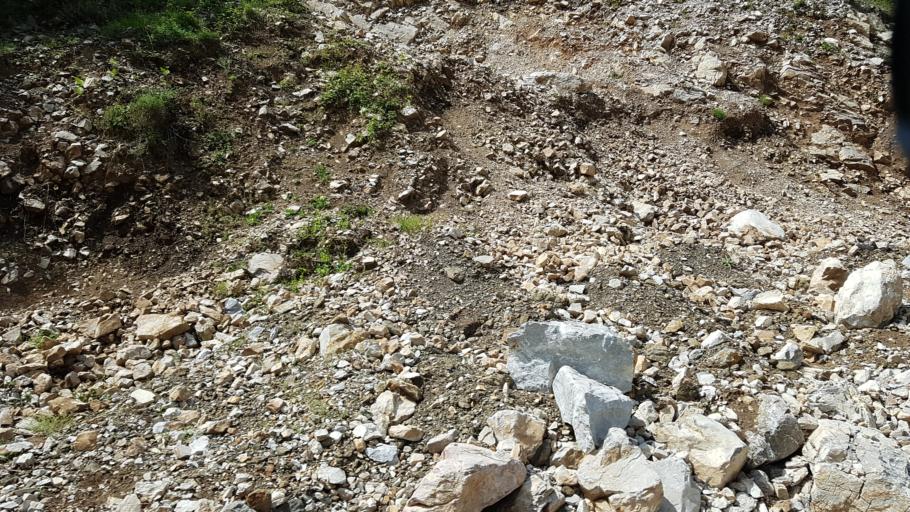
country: AL
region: Shkoder
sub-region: Rrethi i Shkodres
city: Guri i Zi
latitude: 42.1282
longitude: 19.6145
